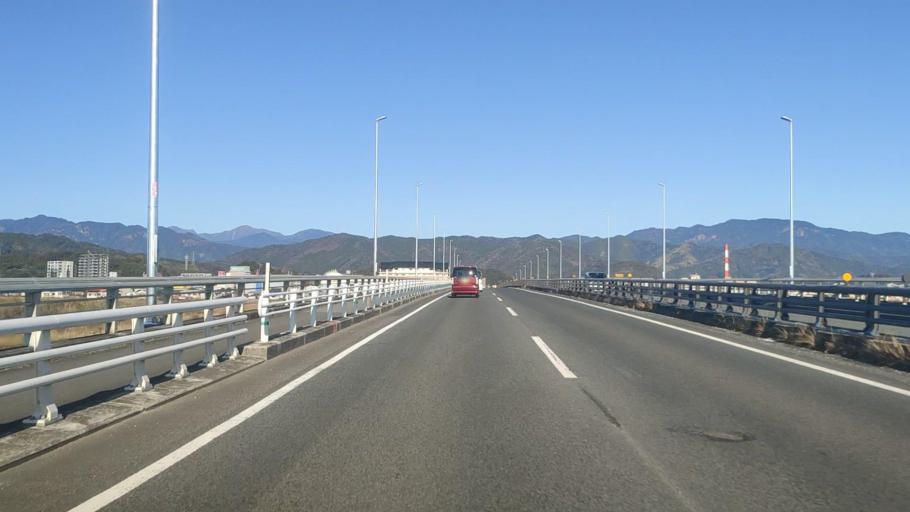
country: JP
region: Miyazaki
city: Nobeoka
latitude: 32.5818
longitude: 131.6807
